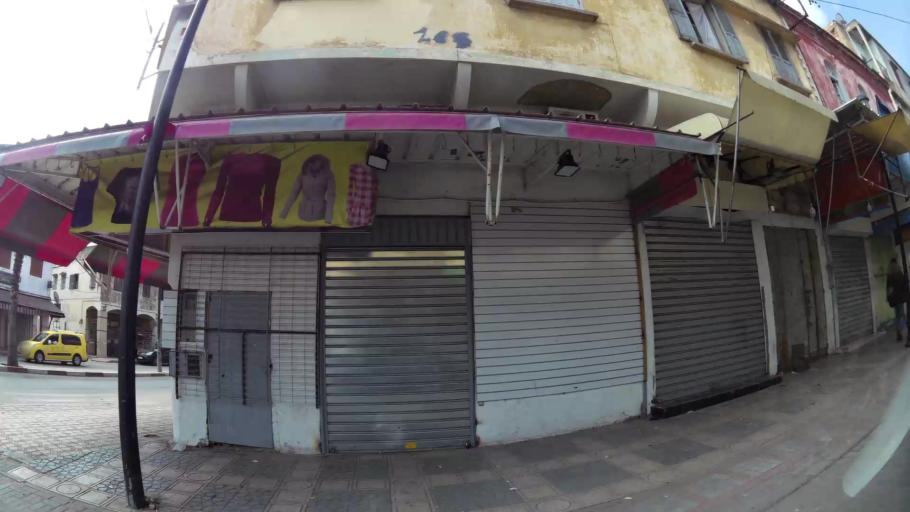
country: MA
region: Gharb-Chrarda-Beni Hssen
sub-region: Kenitra Province
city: Kenitra
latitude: 34.2644
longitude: -6.5618
